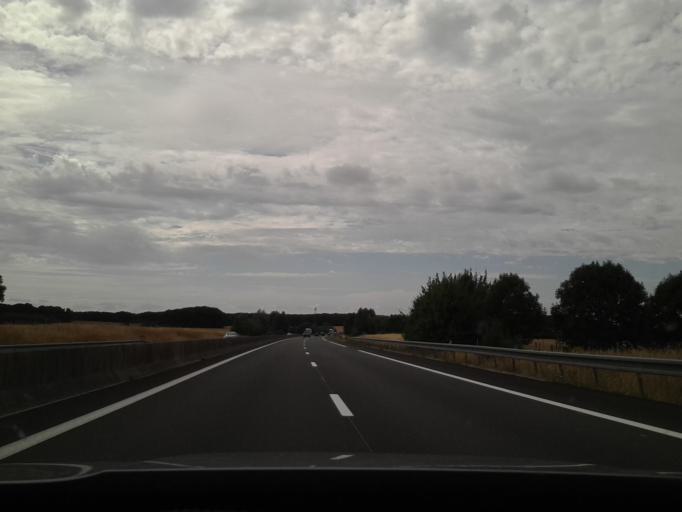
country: FR
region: Pays de la Loire
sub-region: Departement de la Sarthe
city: Beaumont-sur-Sarthe
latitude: 48.3032
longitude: 0.1487
